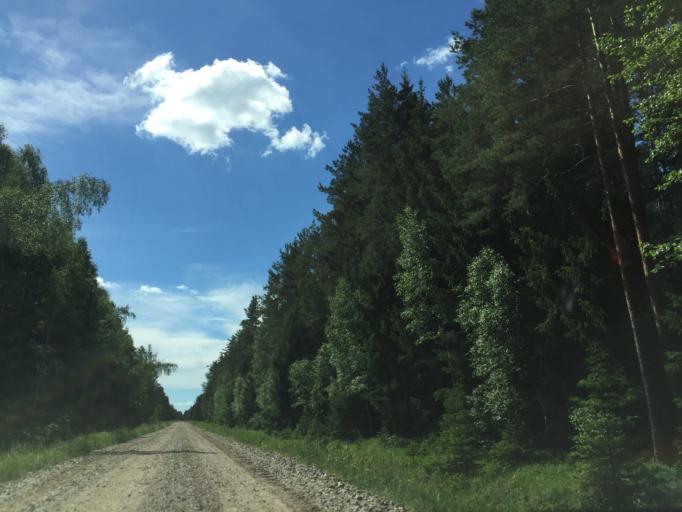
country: LV
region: Ventspils Rajons
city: Piltene
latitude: 57.2647
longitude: 21.8361
